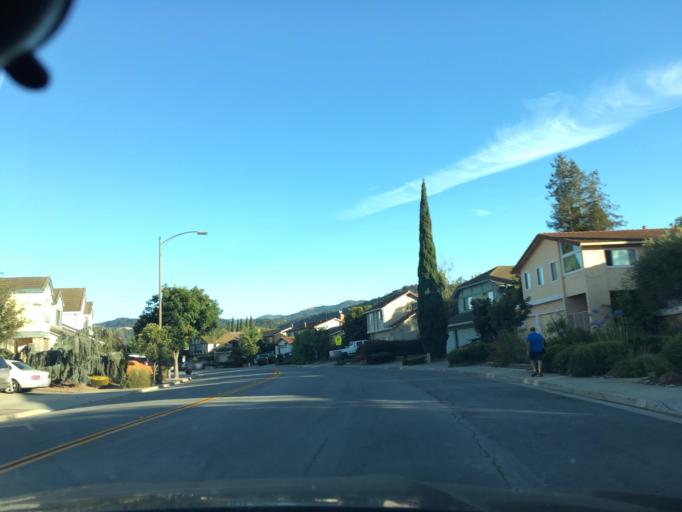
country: US
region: California
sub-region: Santa Clara County
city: Cambrian Park
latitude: 37.2211
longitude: -121.8820
